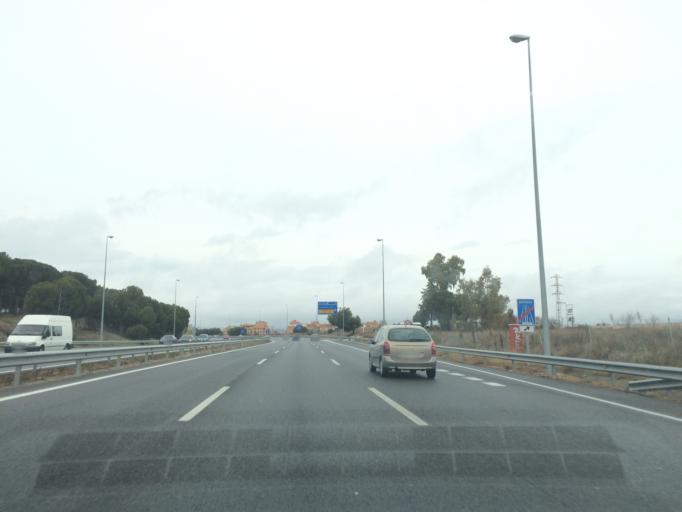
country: ES
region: Madrid
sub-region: Provincia de Madrid
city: Tres Cantos
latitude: 40.5914
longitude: -3.7122
